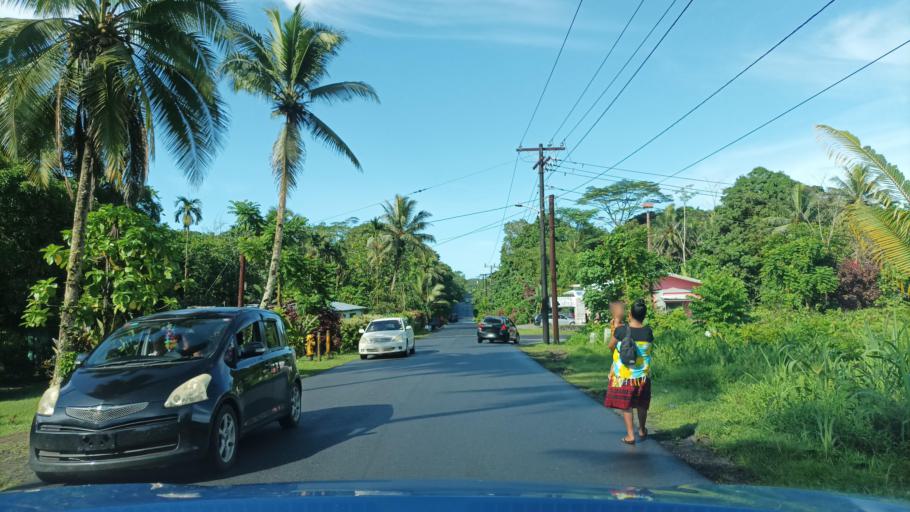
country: FM
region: Pohnpei
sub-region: Sokehs Municipality
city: Palikir - National Government Center
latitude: 6.9232
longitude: 158.1680
